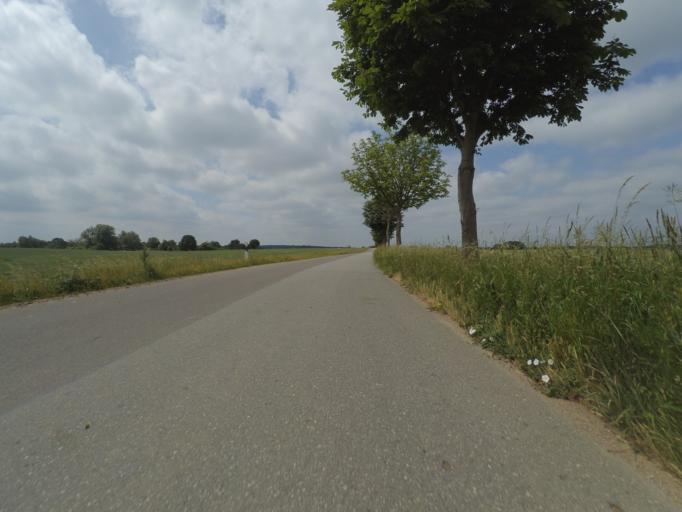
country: DE
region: Mecklenburg-Vorpommern
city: Klink
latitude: 53.4722
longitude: 12.5947
